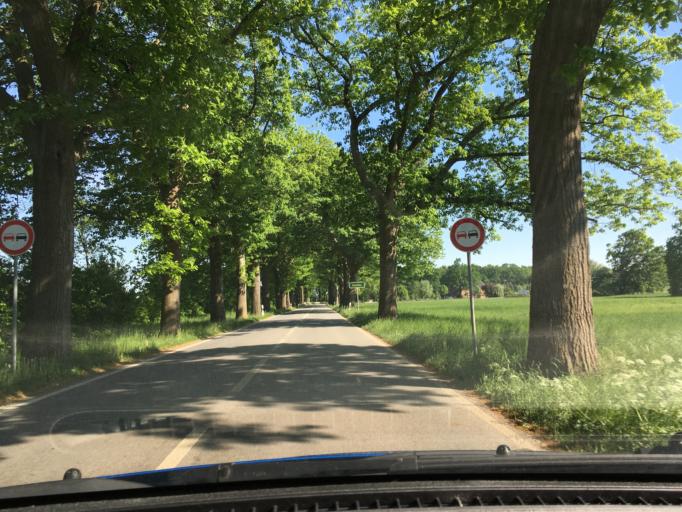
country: DE
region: Lower Saxony
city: Langendorf
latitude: 53.0998
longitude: 11.2821
